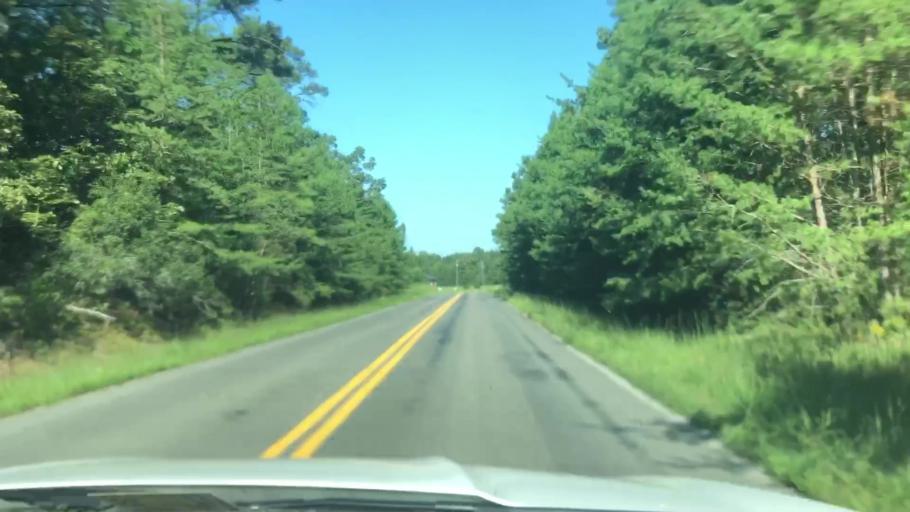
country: US
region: Virginia
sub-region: New Kent County
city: New Kent
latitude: 37.4850
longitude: -76.9300
